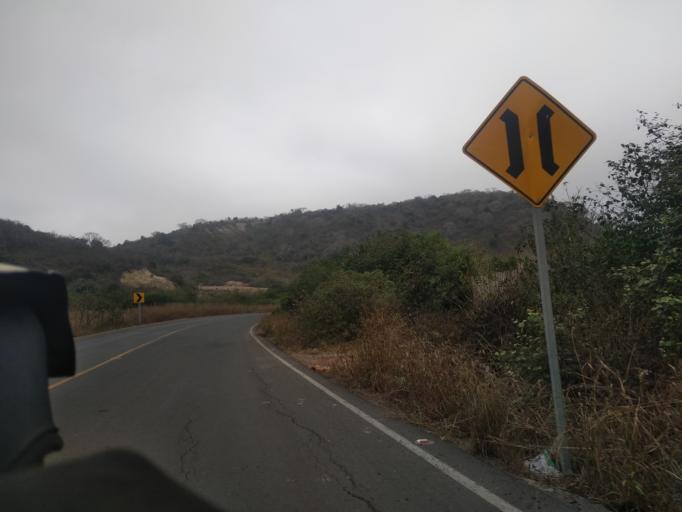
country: EC
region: Manabi
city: Montecristi
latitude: -1.0873
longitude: -80.6871
